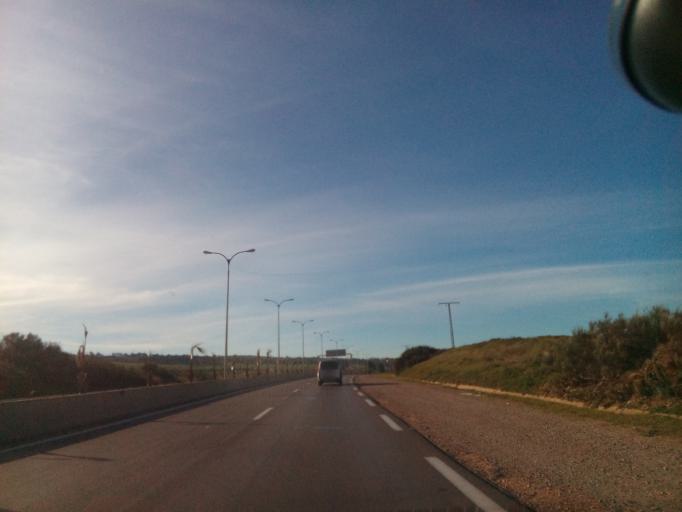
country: DZ
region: Mostaganem
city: Mostaganem
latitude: 35.8272
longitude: -0.0119
